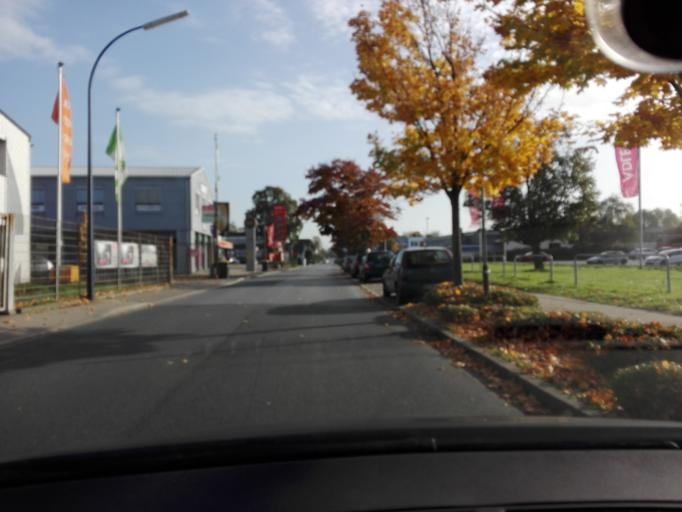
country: DE
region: North Rhine-Westphalia
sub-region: Regierungsbezirk Arnsberg
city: Holzwickede
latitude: 51.5144
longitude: 7.6191
